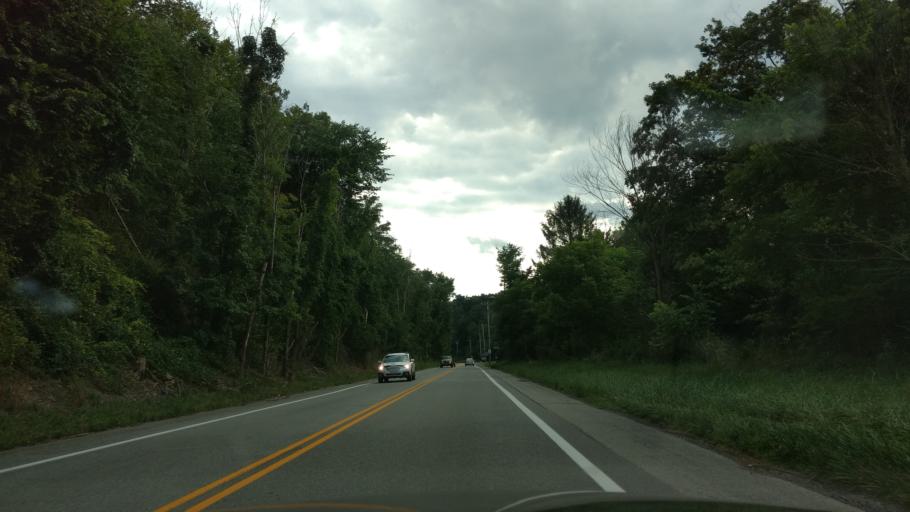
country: US
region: Pennsylvania
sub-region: Allegheny County
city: Plum
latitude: 40.4836
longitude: -79.7015
